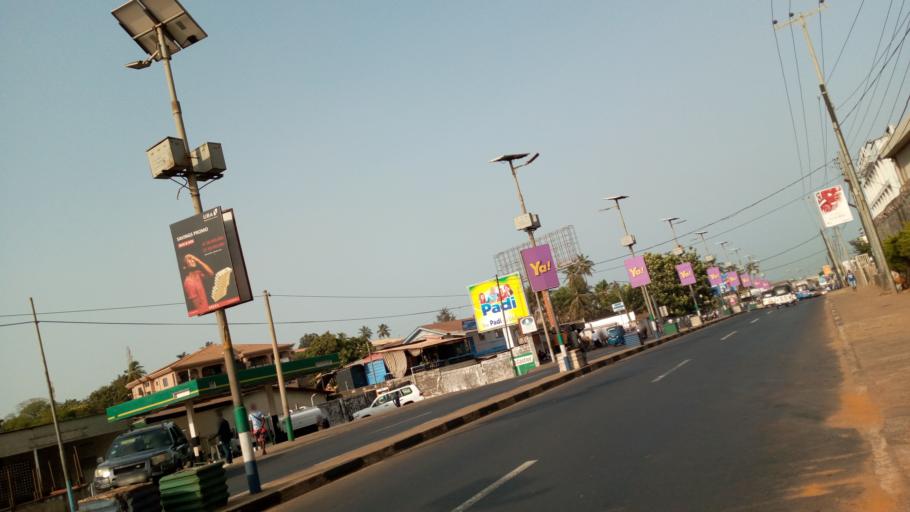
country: SL
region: Western Area
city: Freetown
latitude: 8.4842
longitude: -13.2673
